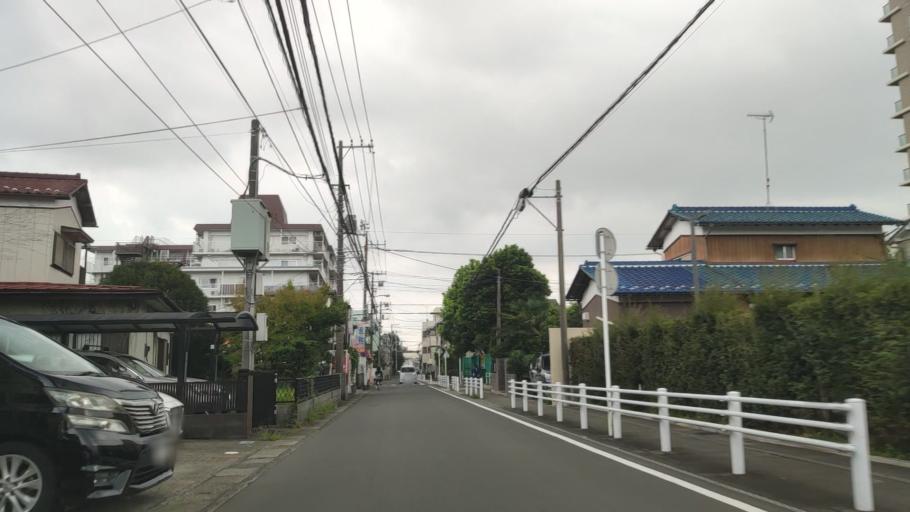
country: JP
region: Kanagawa
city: Minami-rinkan
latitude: 35.4913
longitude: 139.4607
